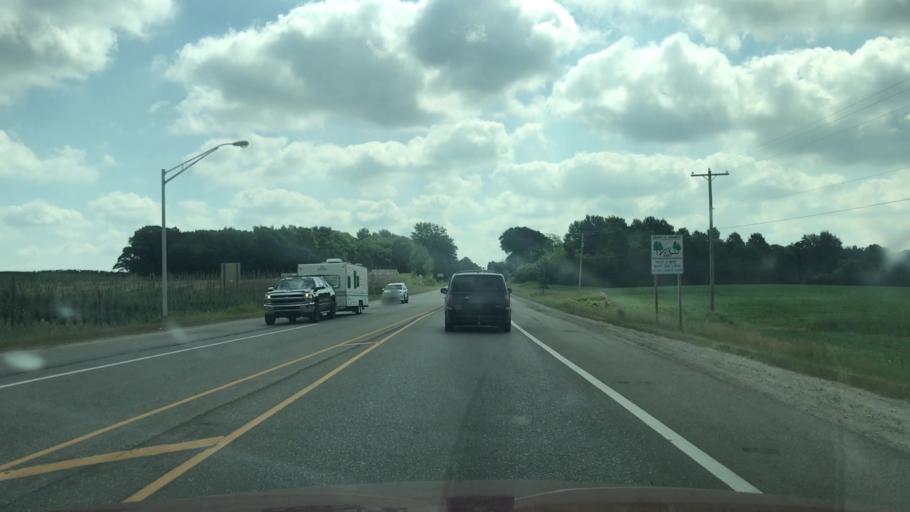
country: US
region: Michigan
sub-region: Kent County
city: Kent City
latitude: 43.2344
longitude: -85.8092
